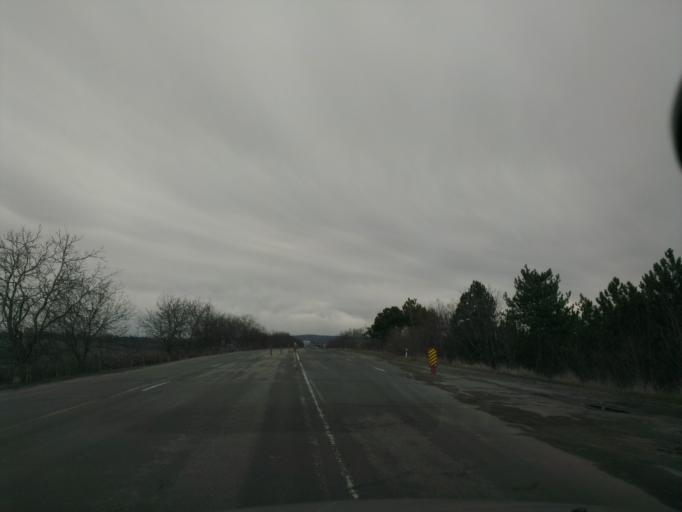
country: MD
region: Laloveni
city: Ialoveni
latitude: 46.9855
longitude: 28.7444
